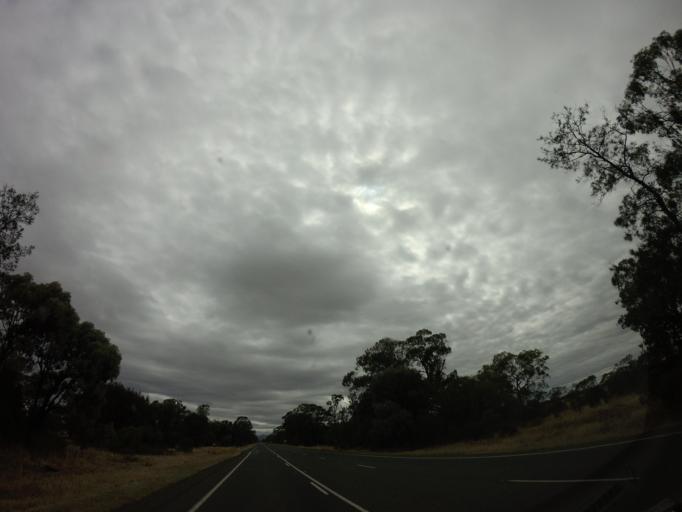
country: AU
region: New South Wales
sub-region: Narrabri
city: Narrabri
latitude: -30.3532
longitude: 149.7494
